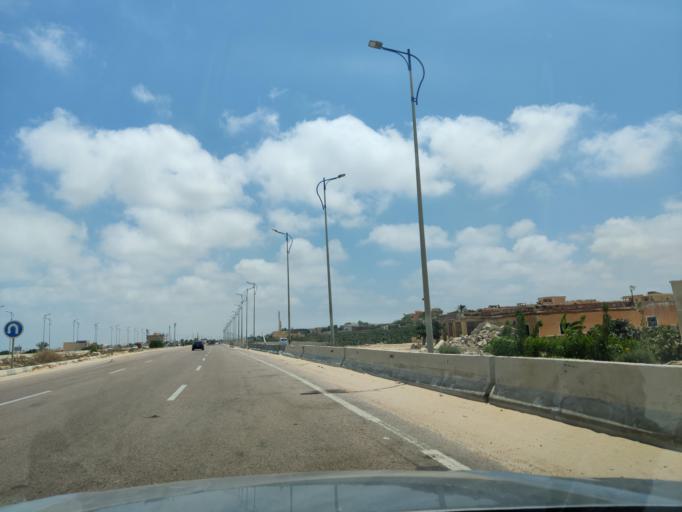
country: EG
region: Alexandria
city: Alexandria
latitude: 30.9627
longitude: 29.5479
